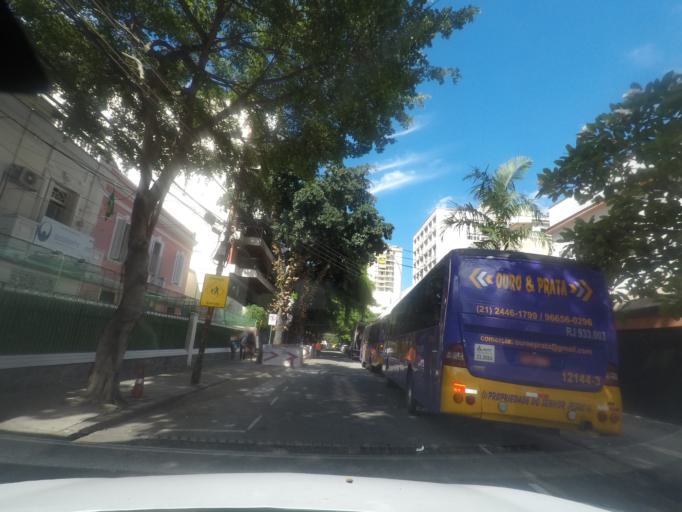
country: BR
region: Rio de Janeiro
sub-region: Rio De Janeiro
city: Rio de Janeiro
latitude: -22.9563
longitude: -43.1931
